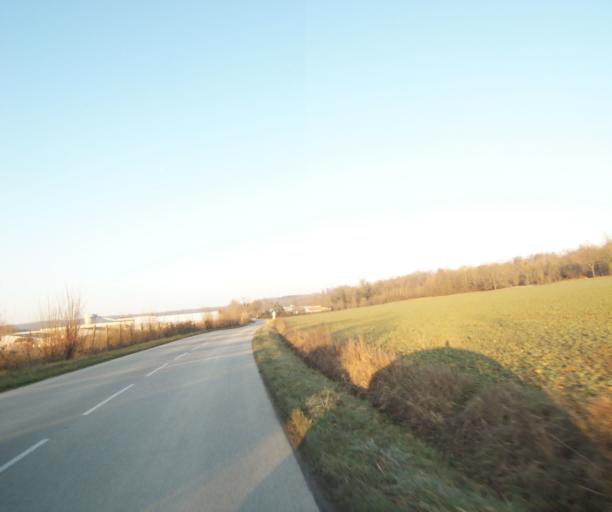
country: FR
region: Champagne-Ardenne
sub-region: Departement de la Haute-Marne
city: Bienville
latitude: 48.5950
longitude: 5.0419
